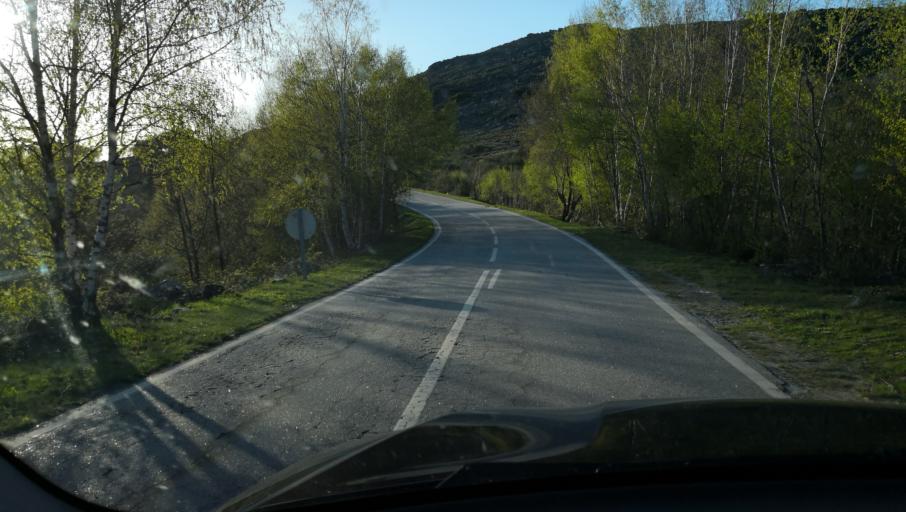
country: PT
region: Vila Real
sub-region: Vila Real
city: Vila Real
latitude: 41.3784
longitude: -7.8133
